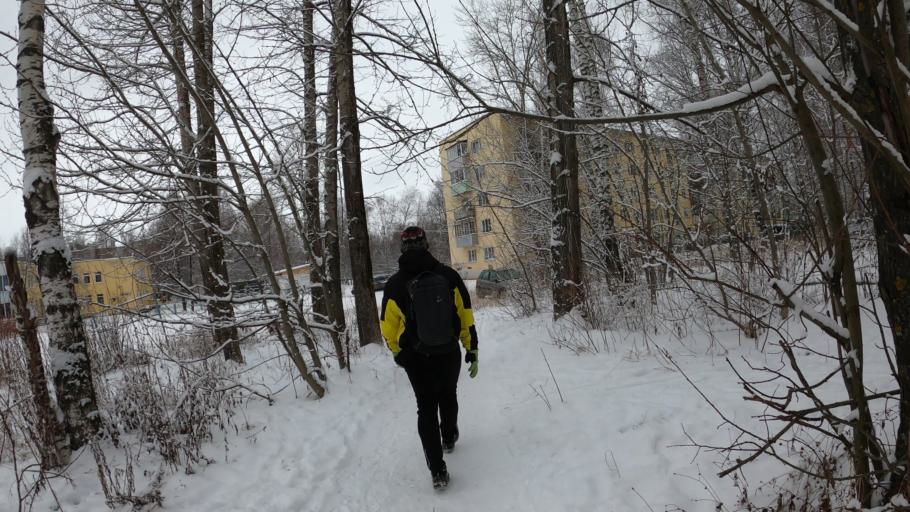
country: RU
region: Jaroslavl
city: Pereslavl'-Zalesskiy
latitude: 56.7534
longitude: 38.8719
